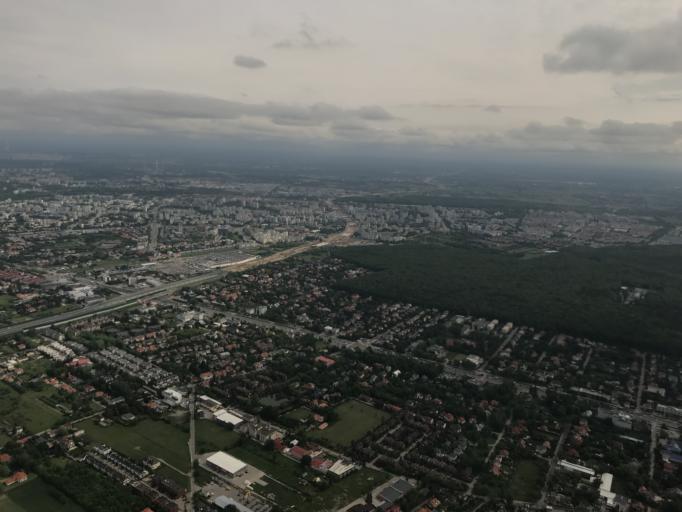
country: PL
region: Masovian Voivodeship
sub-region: Powiat piaseczynski
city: Mysiadlo
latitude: 52.1268
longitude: 21.0003
